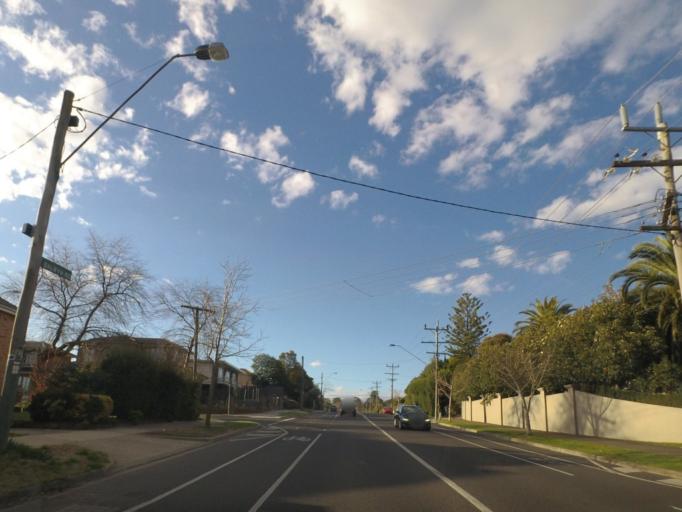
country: AU
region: Victoria
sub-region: Boroondara
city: Balwyn North
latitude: -37.7999
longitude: 145.0838
